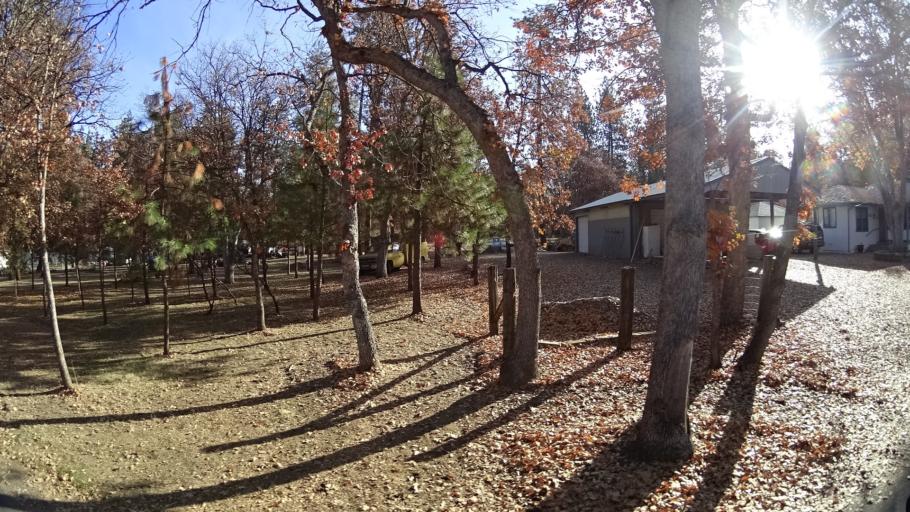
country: US
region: California
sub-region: Siskiyou County
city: Yreka
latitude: 41.6861
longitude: -122.6412
